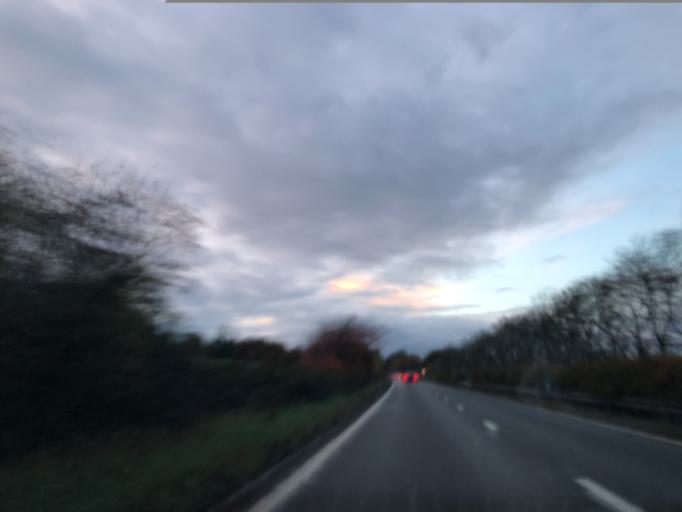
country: GB
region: England
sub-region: Solihull
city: Meriden
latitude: 52.4367
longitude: -1.6097
